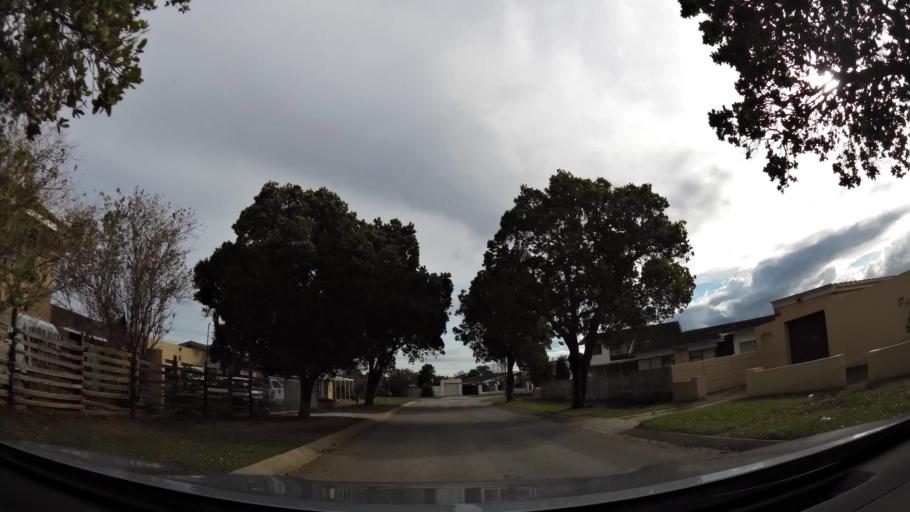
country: ZA
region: Eastern Cape
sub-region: Nelson Mandela Bay Metropolitan Municipality
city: Port Elizabeth
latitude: -33.9382
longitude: 25.5052
